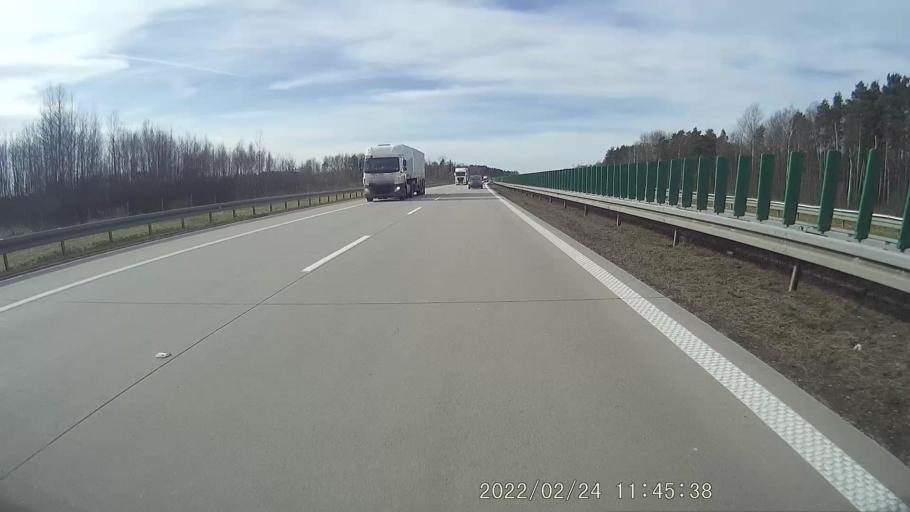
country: PL
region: Lower Silesian Voivodeship
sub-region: Powiat polkowicki
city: Radwanice
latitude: 51.5636
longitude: 15.9370
